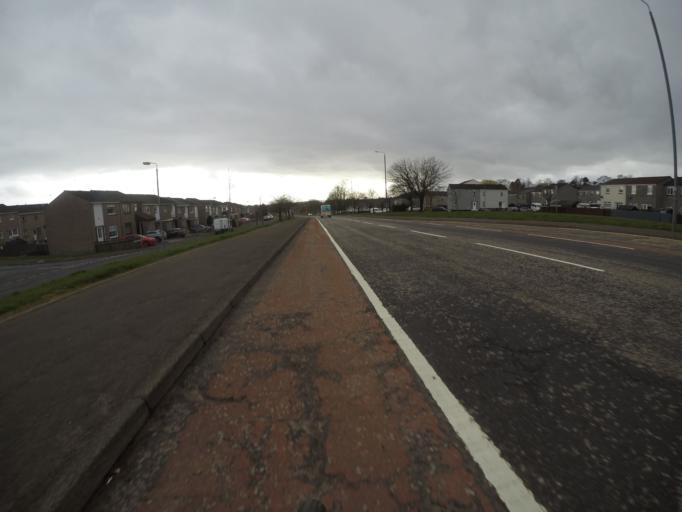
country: GB
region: Scotland
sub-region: East Ayrshire
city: Kilmarnock
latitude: 55.6203
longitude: -4.4739
